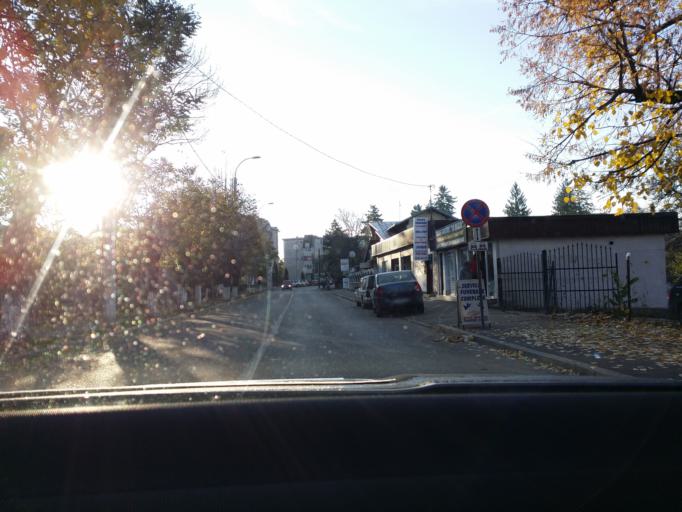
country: RO
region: Prahova
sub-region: Municipiul Campina
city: Campina
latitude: 45.1323
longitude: 25.7328
